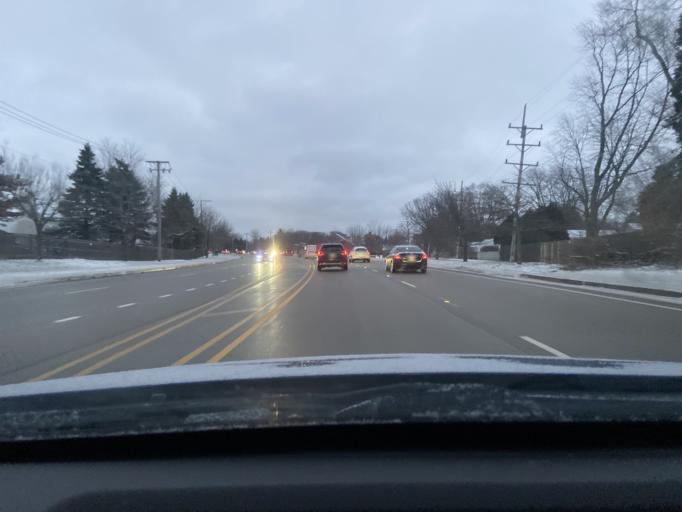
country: US
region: Illinois
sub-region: Lake County
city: Grayslake
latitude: 42.3571
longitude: -88.0426
